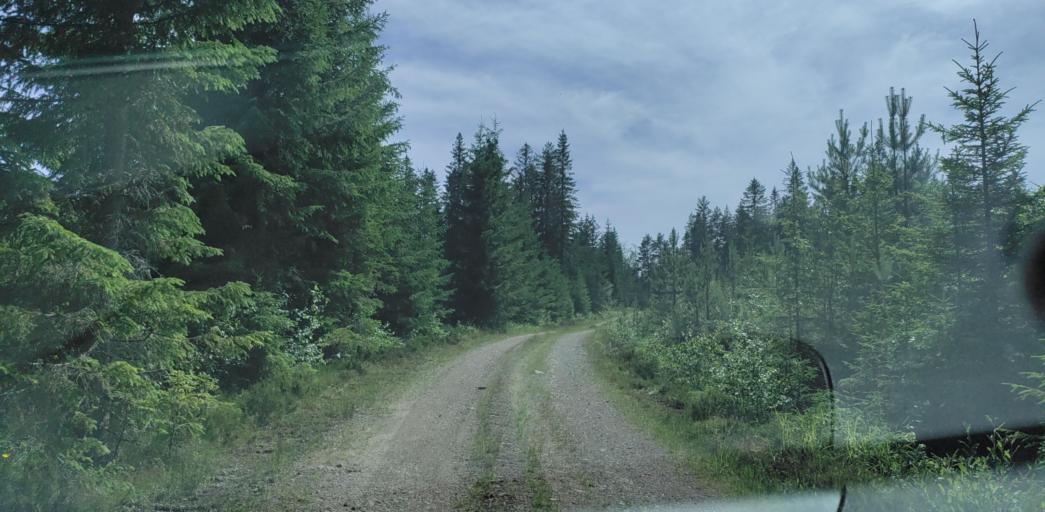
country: SE
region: Vaermland
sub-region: Hagfors Kommun
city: Ekshaerad
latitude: 60.0918
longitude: 13.3766
